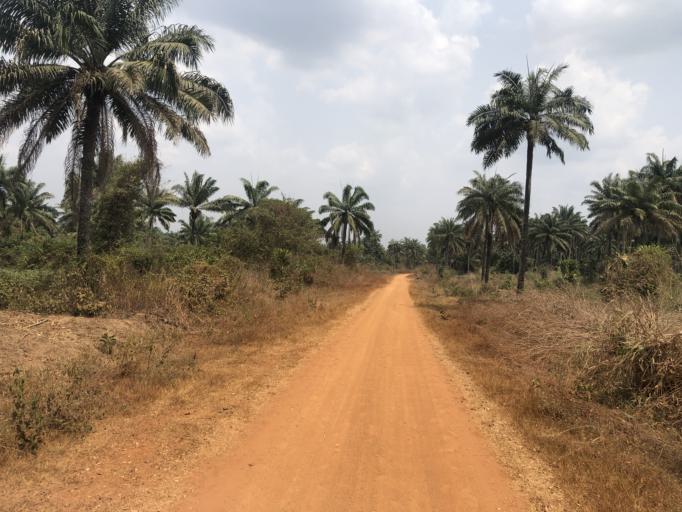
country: NG
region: Osun
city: Bode Osi
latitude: 7.7567
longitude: 4.2578
